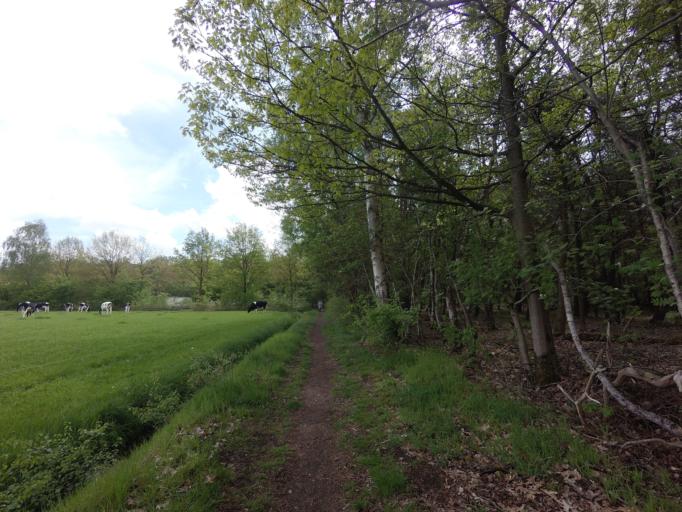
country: NL
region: Overijssel
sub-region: Gemeente Haaksbergen
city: Haaksbergen
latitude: 52.1521
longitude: 6.7820
